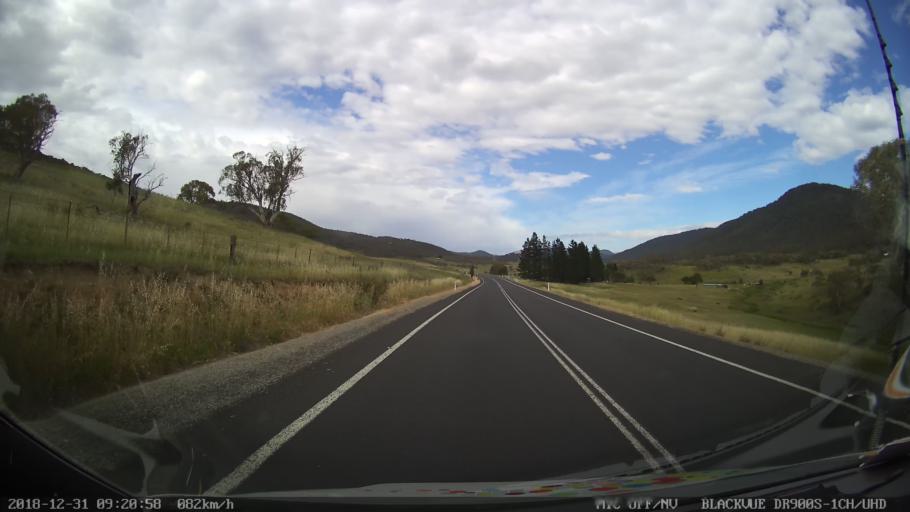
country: AU
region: New South Wales
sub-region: Snowy River
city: Jindabyne
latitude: -36.4253
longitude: 148.5675
